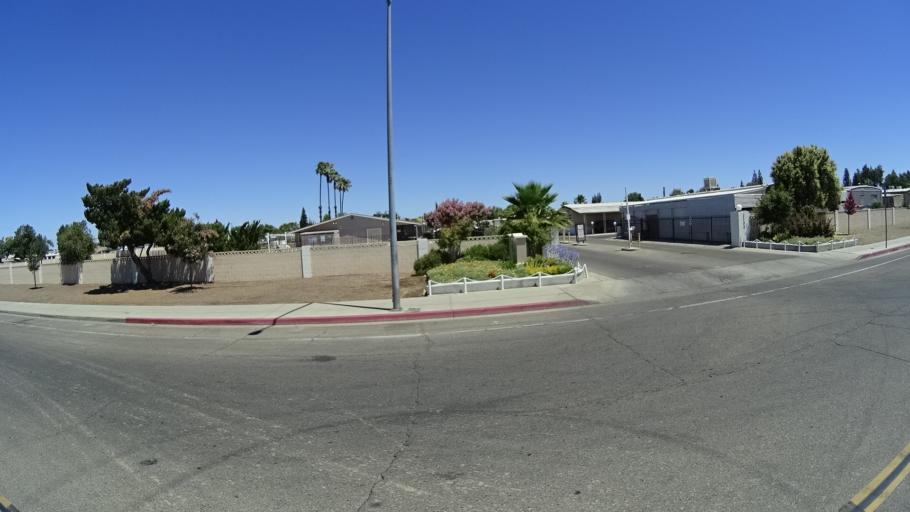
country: US
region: California
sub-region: Fresno County
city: West Park
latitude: 36.7864
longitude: -119.8476
